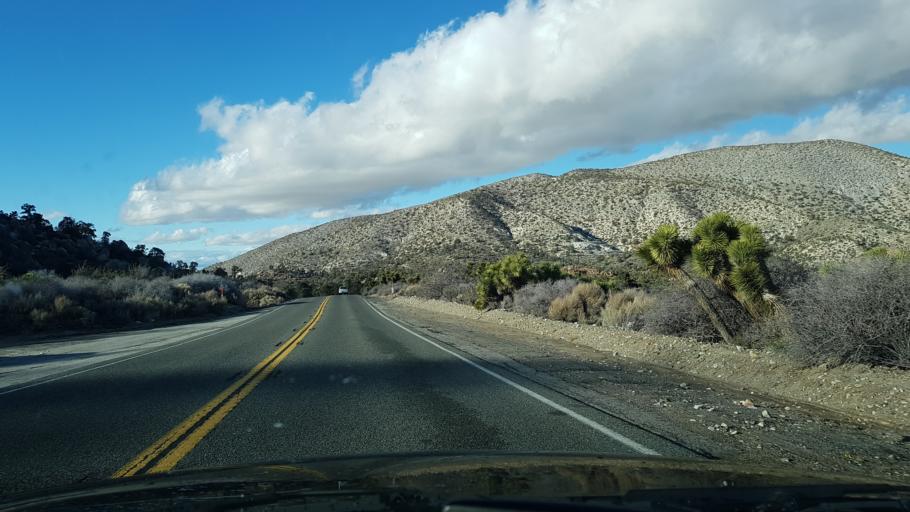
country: US
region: California
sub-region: San Bernardino County
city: Big Bear City
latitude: 34.3195
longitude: -116.8172
